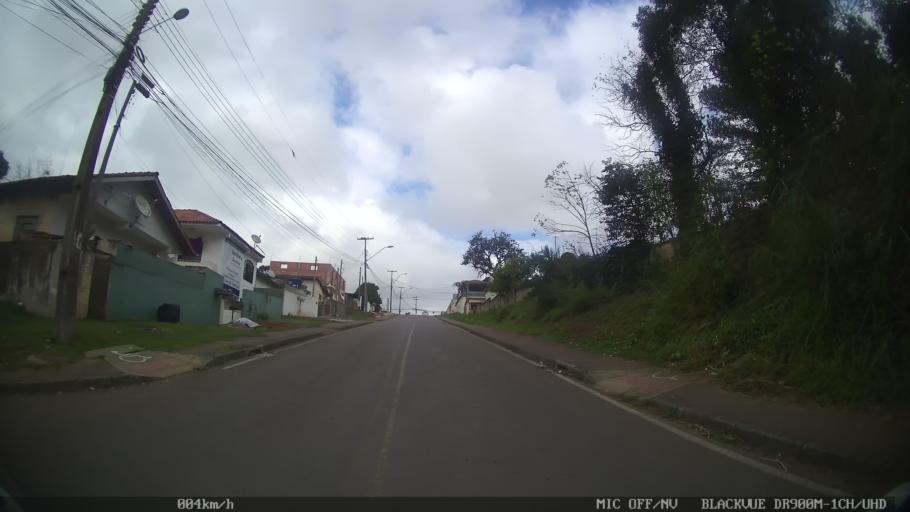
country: BR
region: Parana
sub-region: Colombo
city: Colombo
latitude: -25.3447
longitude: -49.2418
